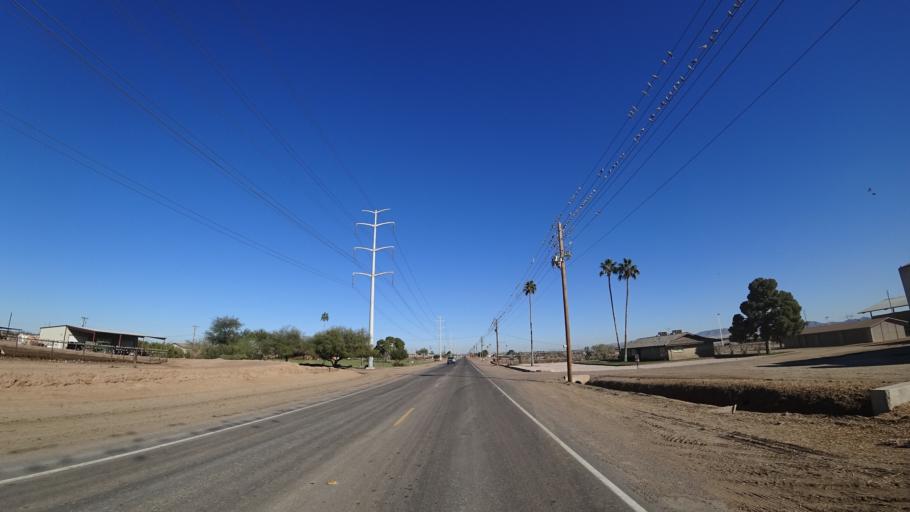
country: US
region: Arizona
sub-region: Maricopa County
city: Tolleson
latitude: 33.4069
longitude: -112.2512
